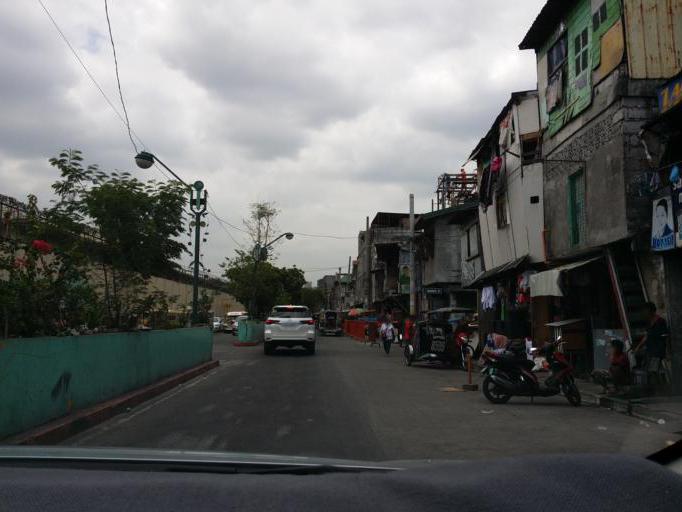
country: PH
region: Metro Manila
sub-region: Makati City
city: Makati City
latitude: 14.5701
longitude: 121.0072
